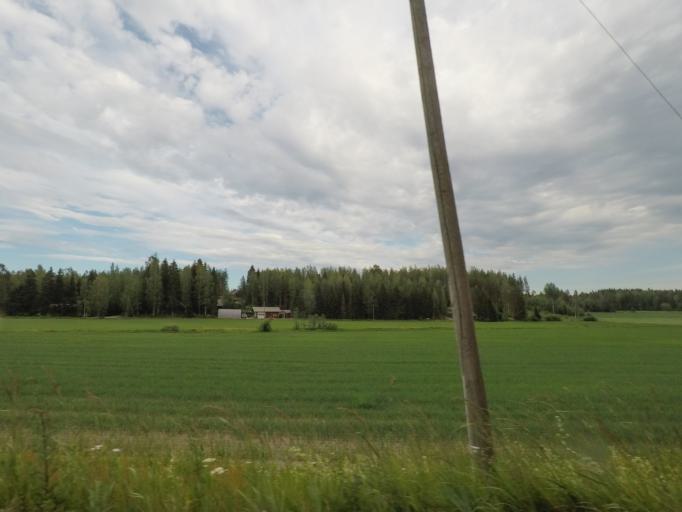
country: FI
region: Uusimaa
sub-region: Porvoo
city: Pukkila
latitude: 60.7704
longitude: 25.4499
